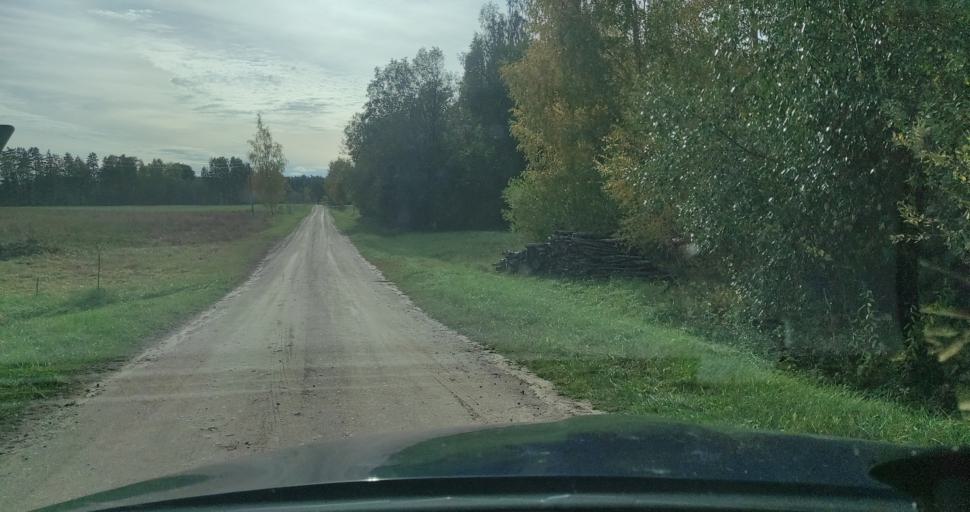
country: LV
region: Jaunpils
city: Jaunpils
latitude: 56.8283
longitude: 22.9692
